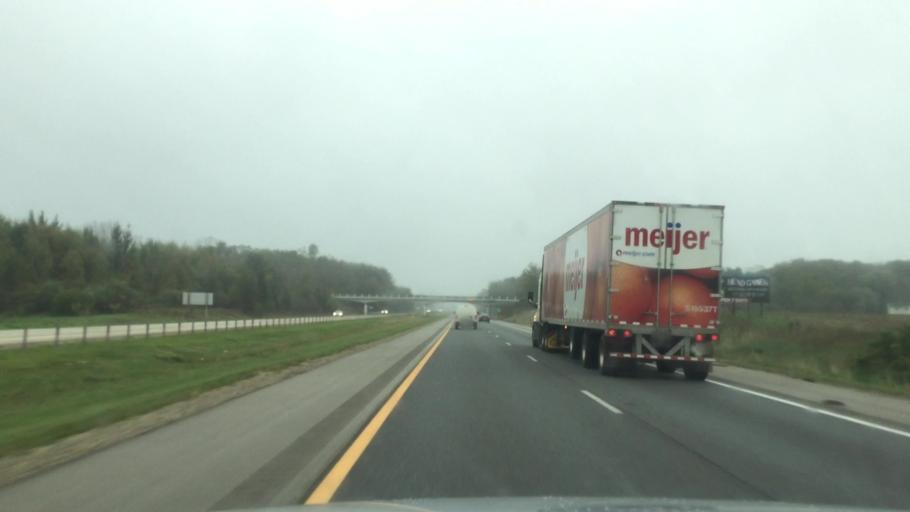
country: US
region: Michigan
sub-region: Berrien County
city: Watervliet
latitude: 42.1826
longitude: -86.2269
